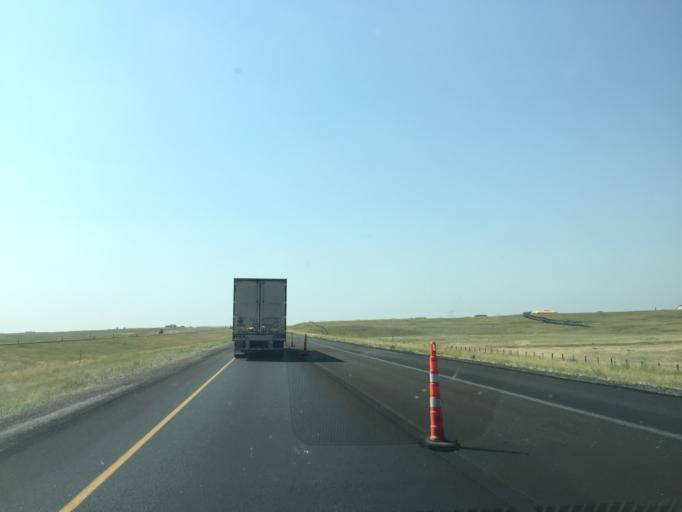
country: US
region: Wyoming
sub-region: Laramie County
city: Ranchettes
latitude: 41.3100
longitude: -104.8575
